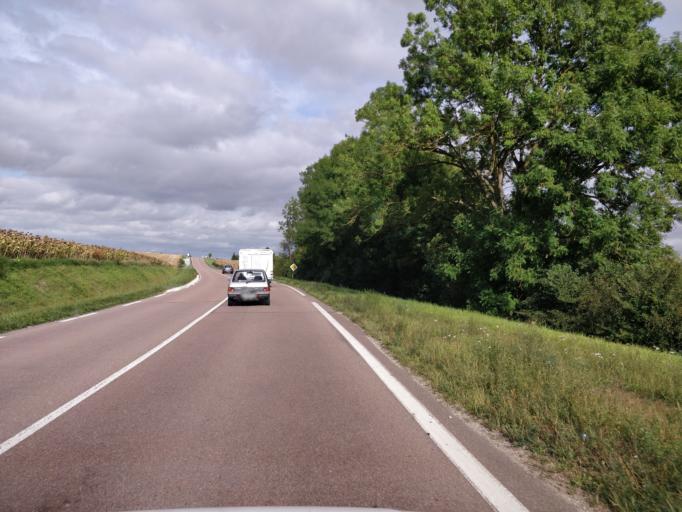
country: FR
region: Champagne-Ardenne
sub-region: Departement de l'Aube
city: Aix-en-Othe
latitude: 48.2448
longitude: 3.7088
